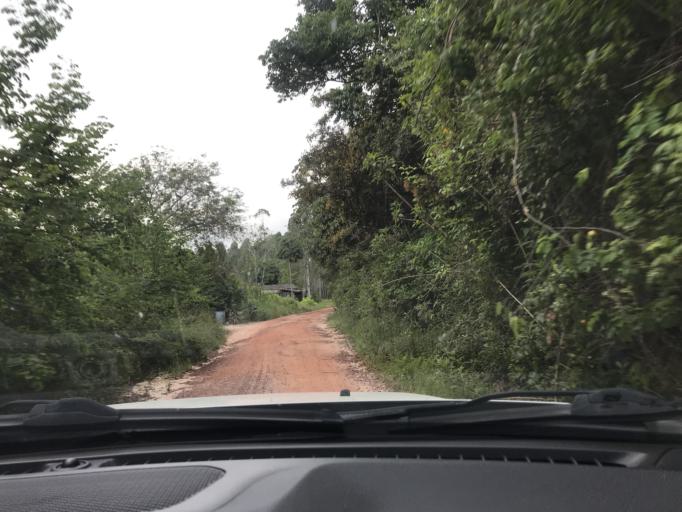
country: BR
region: Bahia
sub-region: Entre Rios
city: Entre Rios
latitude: -12.0971
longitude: -38.1907
